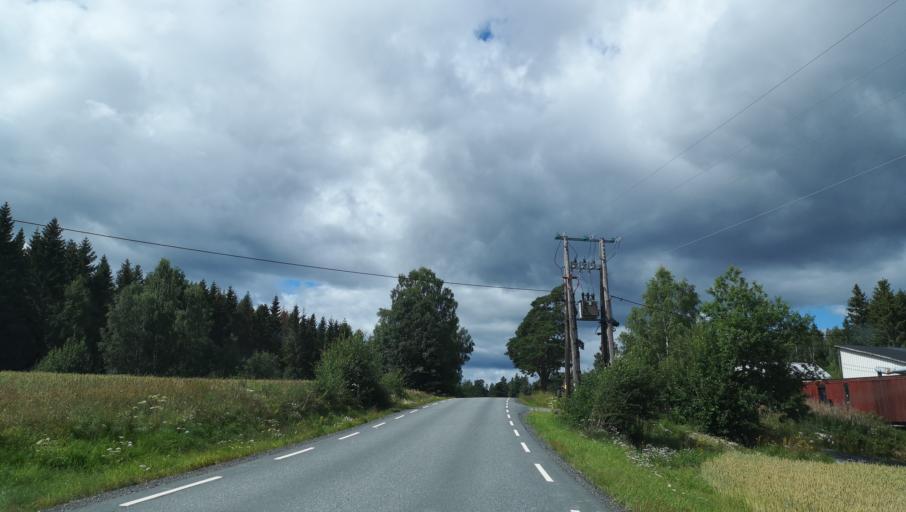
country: NO
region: Ostfold
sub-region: Hobol
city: Tomter
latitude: 59.6727
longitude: 10.9794
